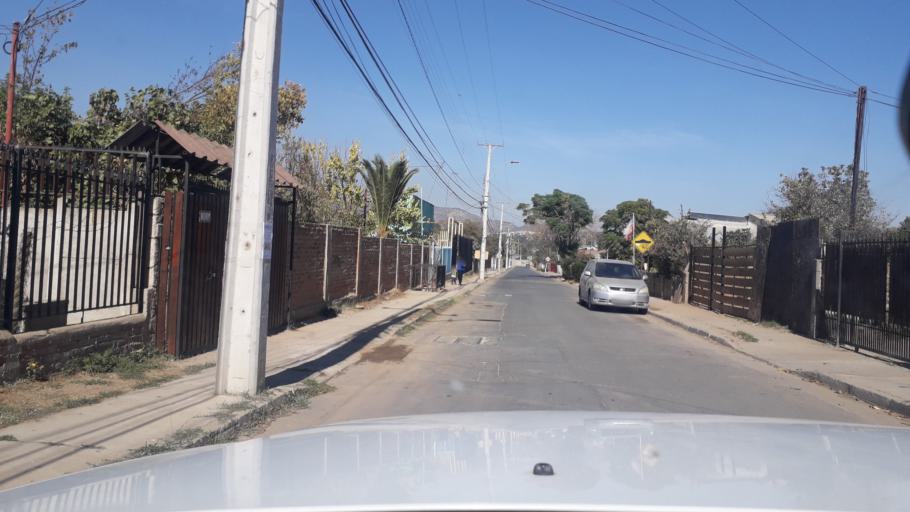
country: CL
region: Valparaiso
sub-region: Provincia de Marga Marga
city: Villa Alemana
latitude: -33.0373
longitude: -71.3548
